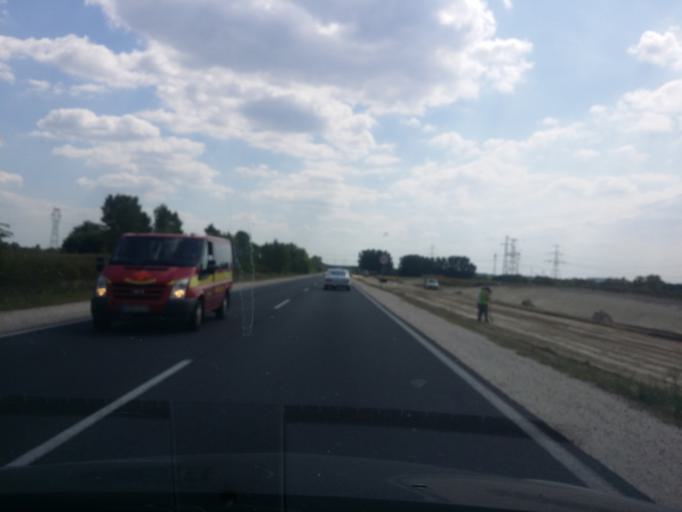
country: HU
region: Pest
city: Szod
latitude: 47.7004
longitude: 19.1685
